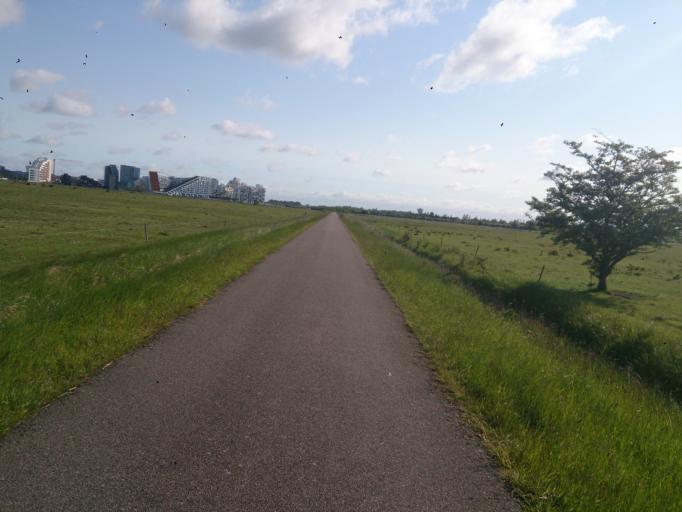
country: DK
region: Capital Region
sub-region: Tarnby Kommune
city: Tarnby
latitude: 55.6087
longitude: 12.5646
